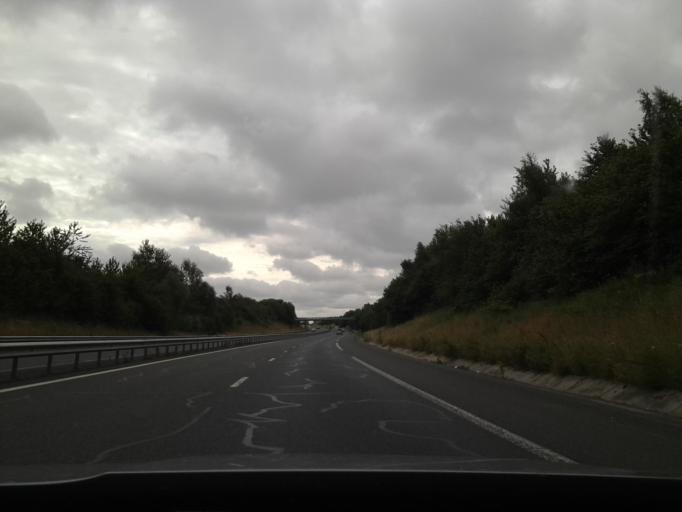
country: FR
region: Lower Normandy
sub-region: Departement du Calvados
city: Port-en-Bessin-Huppain
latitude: 49.3090
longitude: -0.8256
